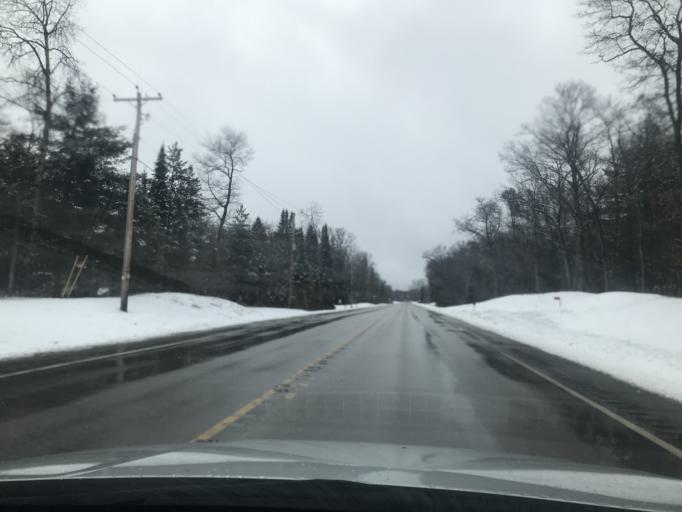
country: US
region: Wisconsin
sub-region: Marinette County
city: Peshtigo
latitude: 45.1674
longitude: -87.7298
